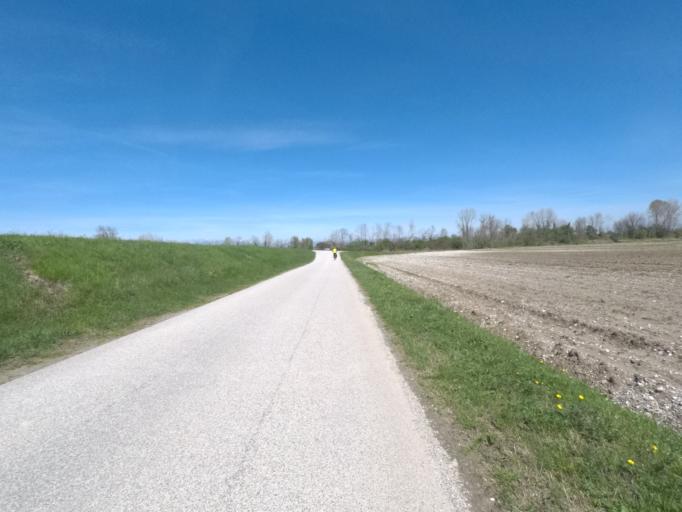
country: IT
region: Friuli Venezia Giulia
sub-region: Provincia di Udine
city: Camino al Tagliamento
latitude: 45.9576
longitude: 12.9129
